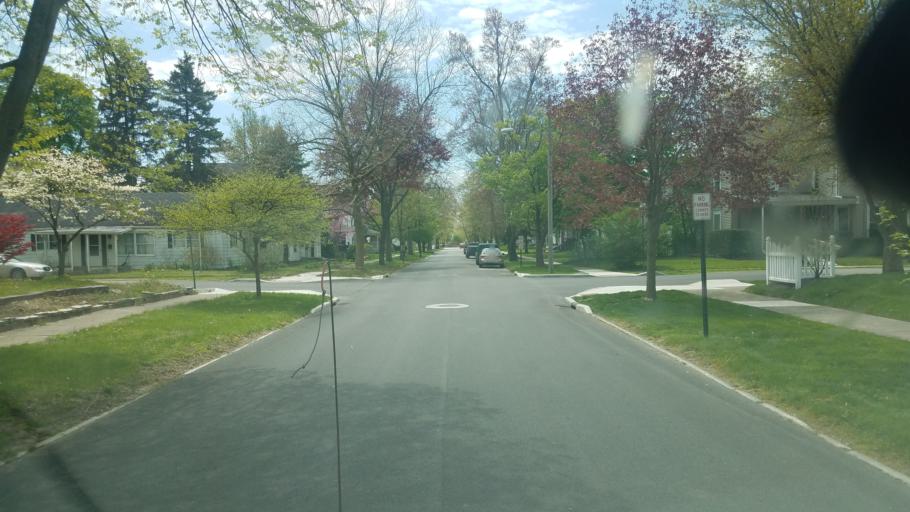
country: US
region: Ohio
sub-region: Hardin County
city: Ada
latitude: 40.7646
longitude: -83.8216
